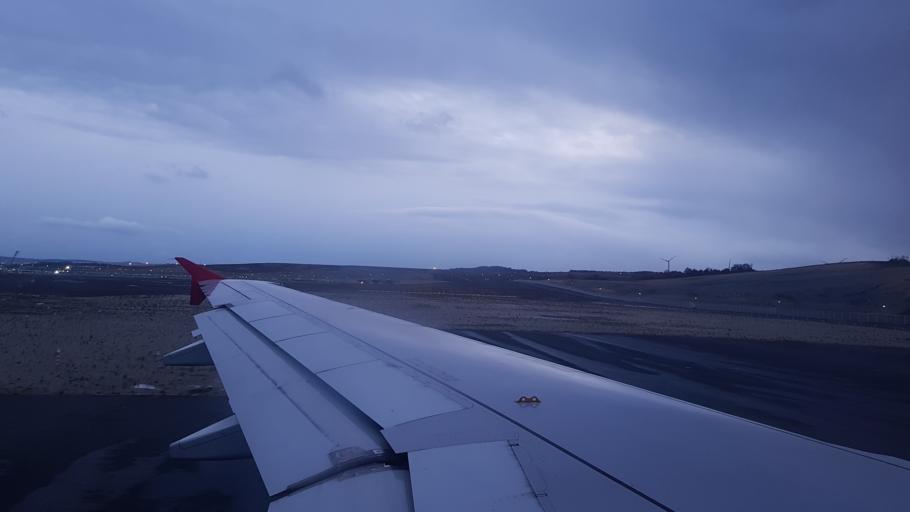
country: TR
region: Istanbul
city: Durusu
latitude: 41.2649
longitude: 28.7078
